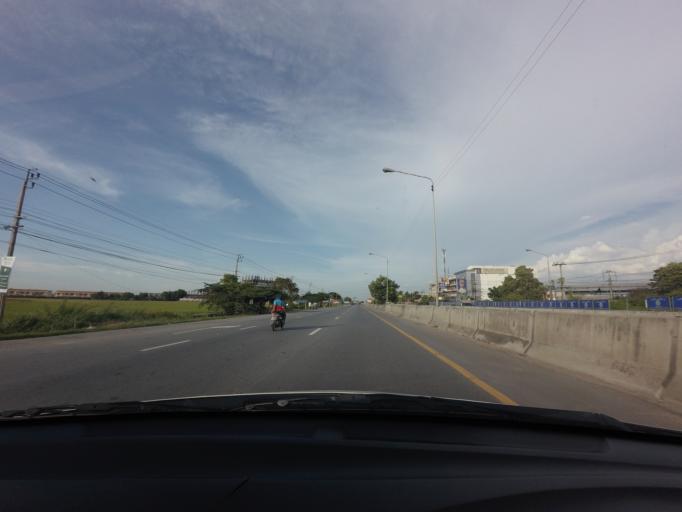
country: TH
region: Nonthaburi
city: Bang Bua Thong
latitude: 13.9428
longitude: 100.4252
